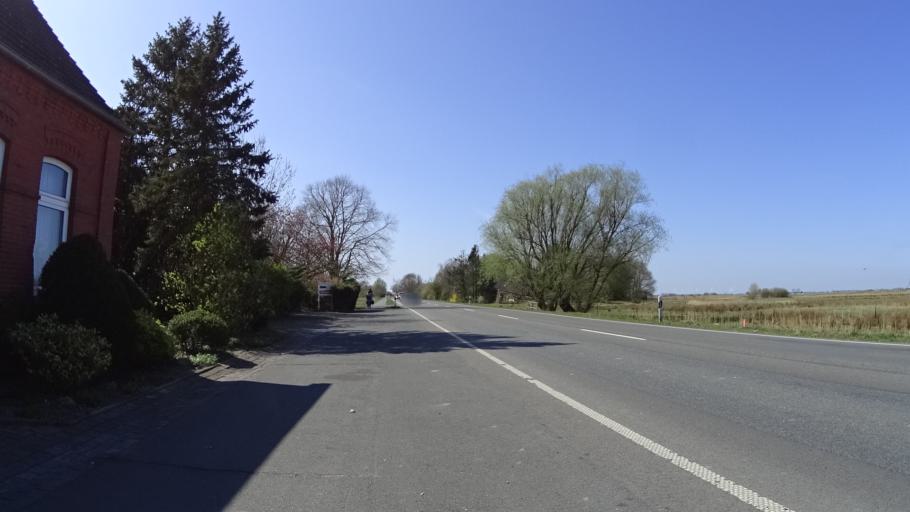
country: DE
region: Lower Saxony
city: Leer
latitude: 53.2126
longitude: 7.4113
